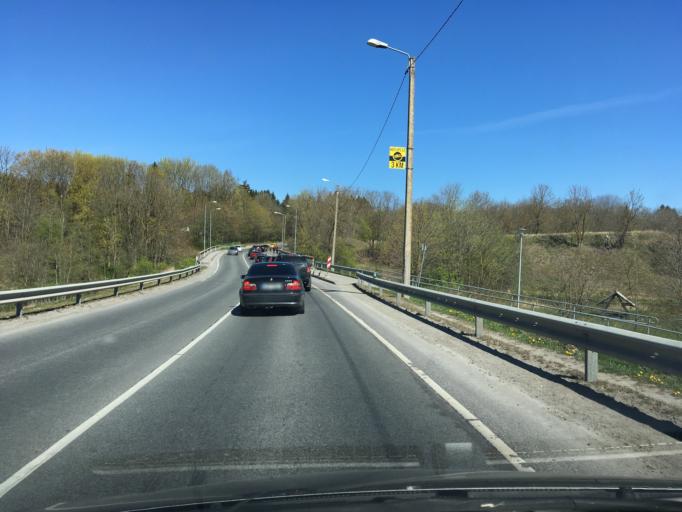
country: EE
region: Harju
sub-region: Tallinna linn
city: Kose
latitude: 59.4574
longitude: 24.9010
